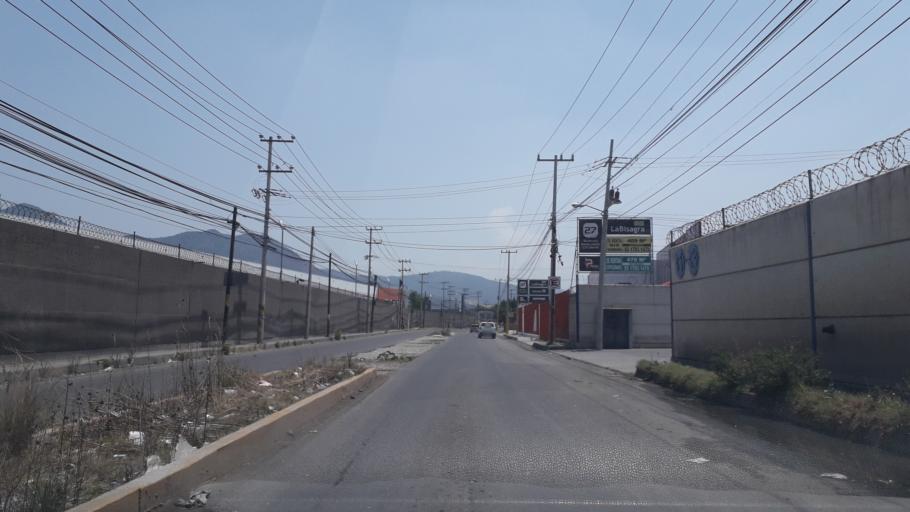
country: MX
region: Mexico
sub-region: Tultitlan
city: Colonia Lazaro Cardenas (Los Hornos)
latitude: 19.6309
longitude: -99.1529
